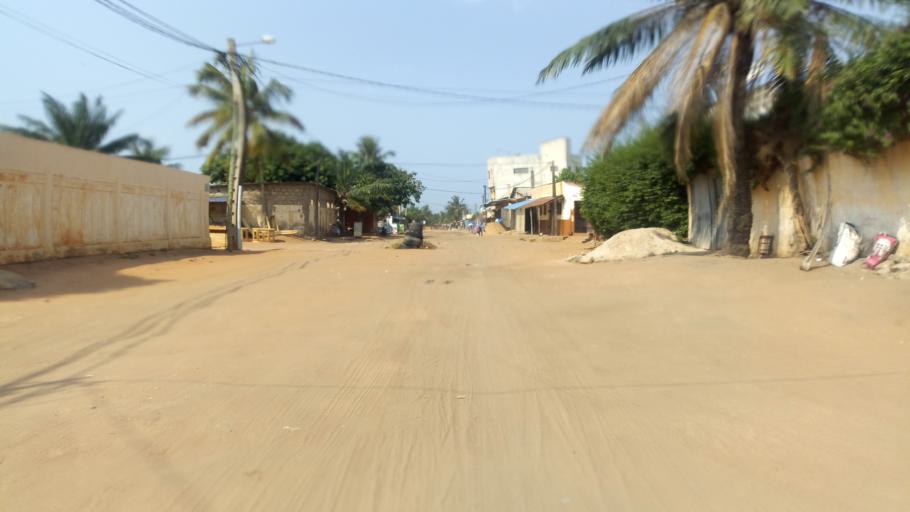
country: TG
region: Maritime
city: Lome
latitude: 6.1893
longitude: 1.1799
